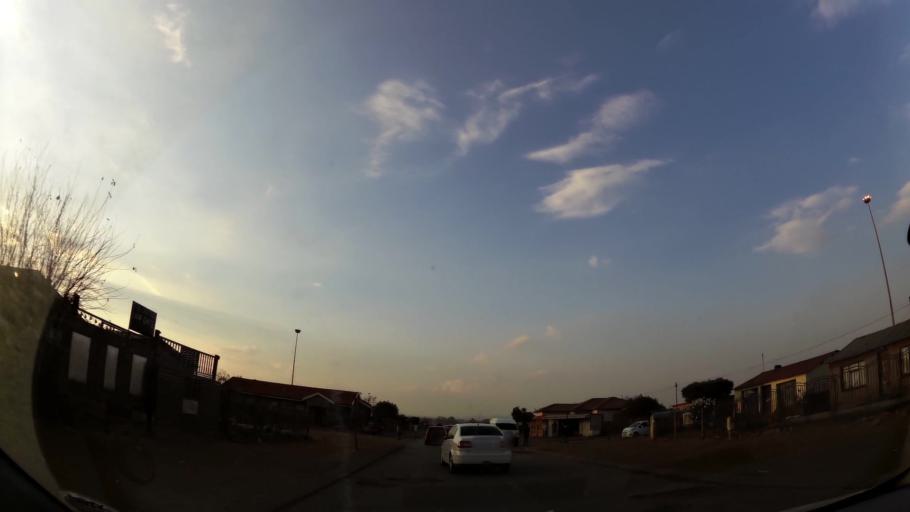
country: ZA
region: Gauteng
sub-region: City of Johannesburg Metropolitan Municipality
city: Orange Farm
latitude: -26.5591
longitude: 27.8614
